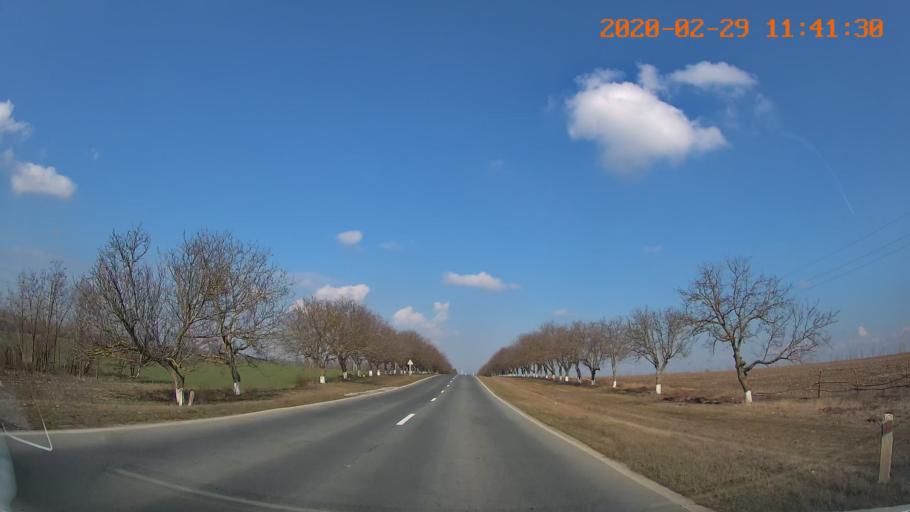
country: MD
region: Rezina
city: Saharna
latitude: 47.6723
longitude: 29.0162
